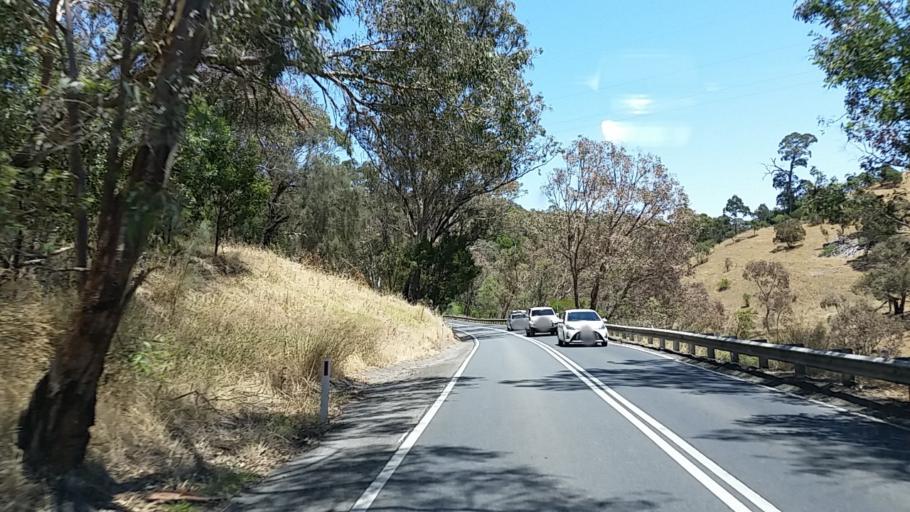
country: AU
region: South Australia
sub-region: Tea Tree Gully
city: Golden Grove
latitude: -34.8247
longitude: 138.7508
